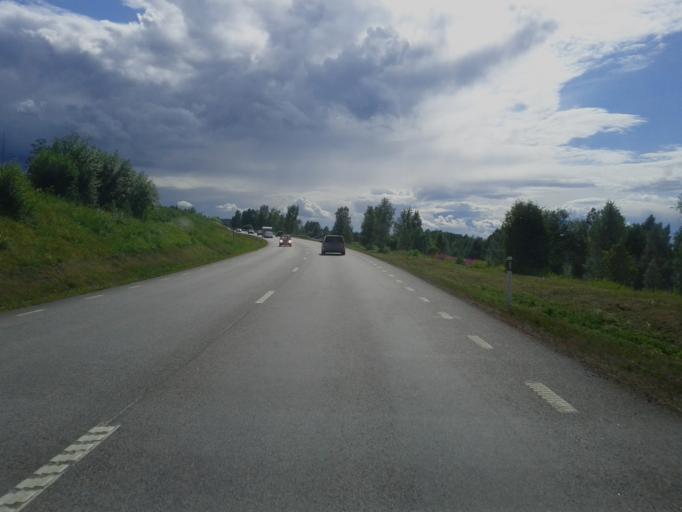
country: SE
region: Dalarna
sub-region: Rattviks Kommun
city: Raettvik
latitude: 60.8737
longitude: 15.1046
